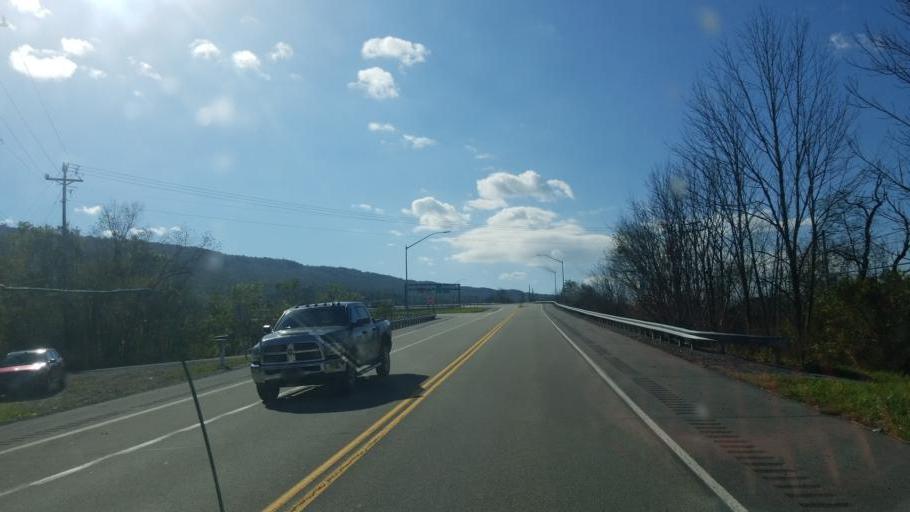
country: US
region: Pennsylvania
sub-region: Blair County
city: Claysburg
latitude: 40.2624
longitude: -78.4602
